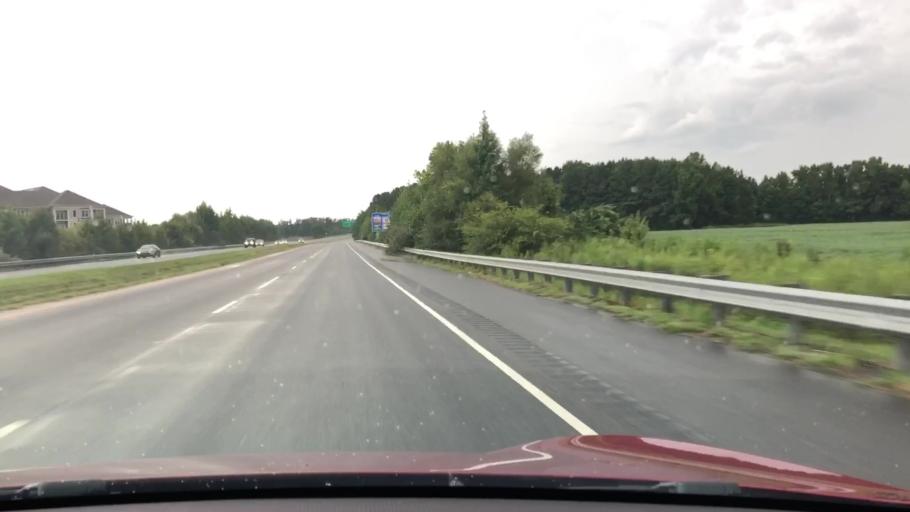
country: US
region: North Carolina
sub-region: Currituck County
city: Moyock
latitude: 36.6507
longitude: -76.2252
